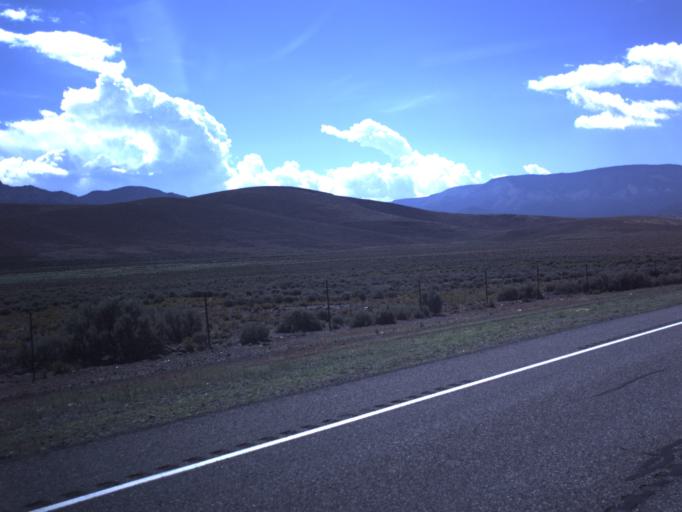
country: US
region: Utah
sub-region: Piute County
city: Junction
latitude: 38.2711
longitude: -112.2227
